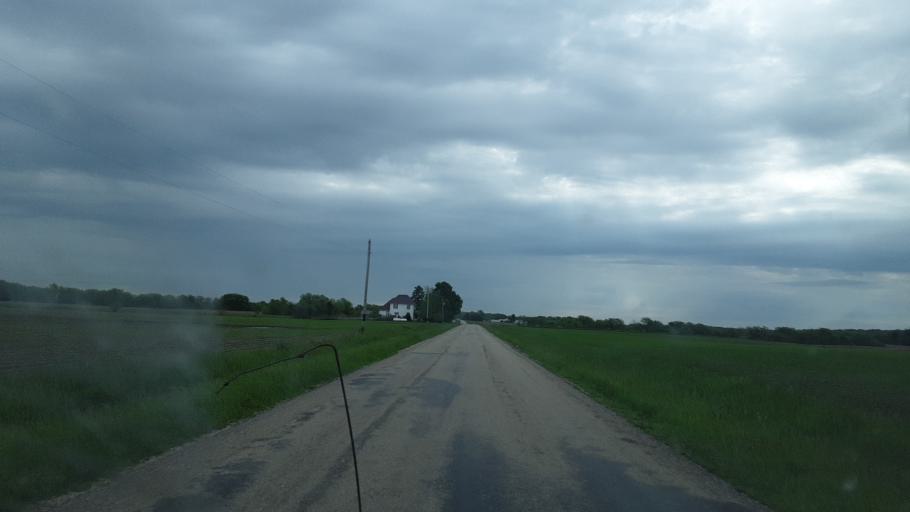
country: US
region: Illinois
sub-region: Fulton County
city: Astoria
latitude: 40.3647
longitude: -90.4728
